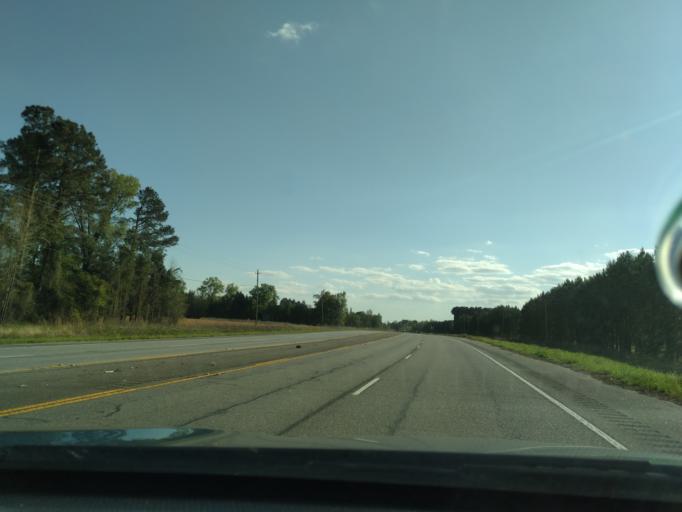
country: US
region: South Carolina
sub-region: Williamsburg County
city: Kingstree
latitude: 33.6313
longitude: -79.9209
